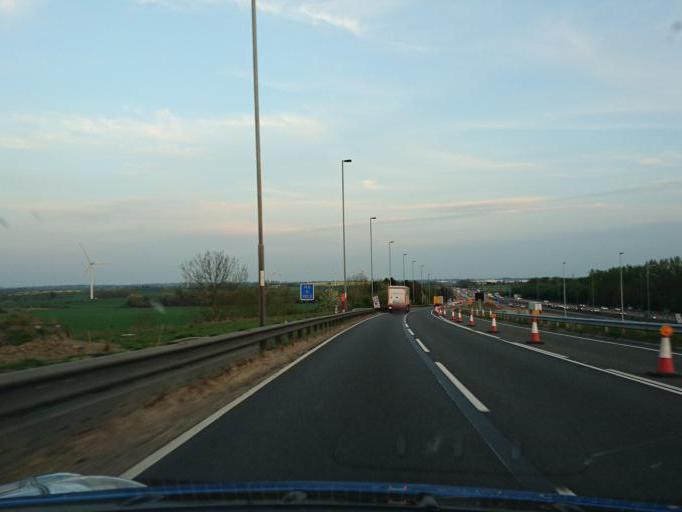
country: GB
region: England
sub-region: Leicestershire
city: Lutterworth
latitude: 52.4015
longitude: -1.1745
